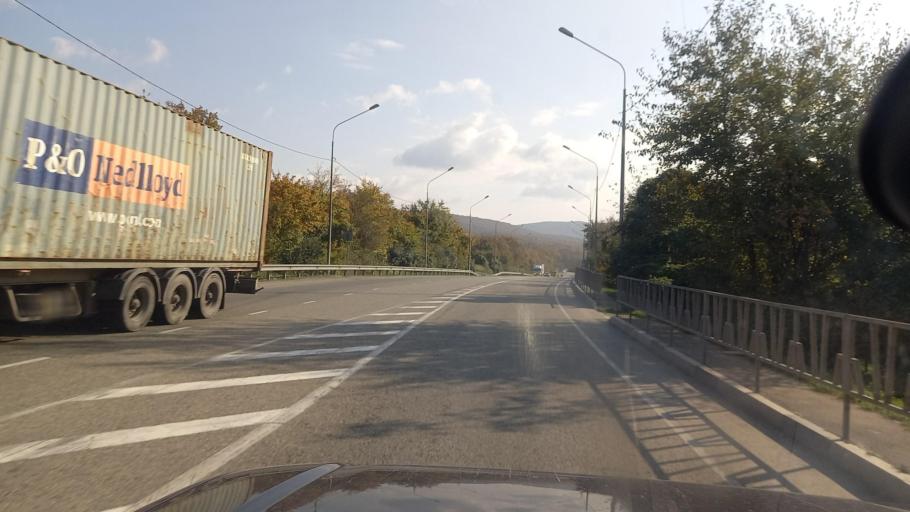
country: RU
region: Krasnodarskiy
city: Verkhnebakanskiy
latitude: 44.8458
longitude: 37.6787
